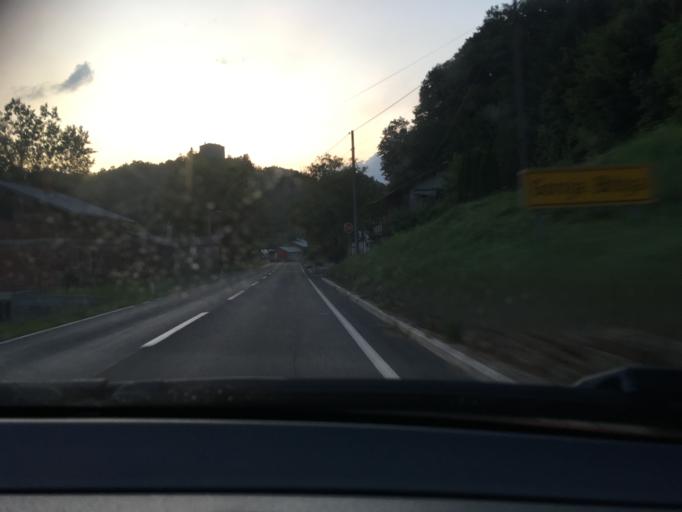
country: SI
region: Pivka
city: Pivka
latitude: 45.6028
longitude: 14.1918
